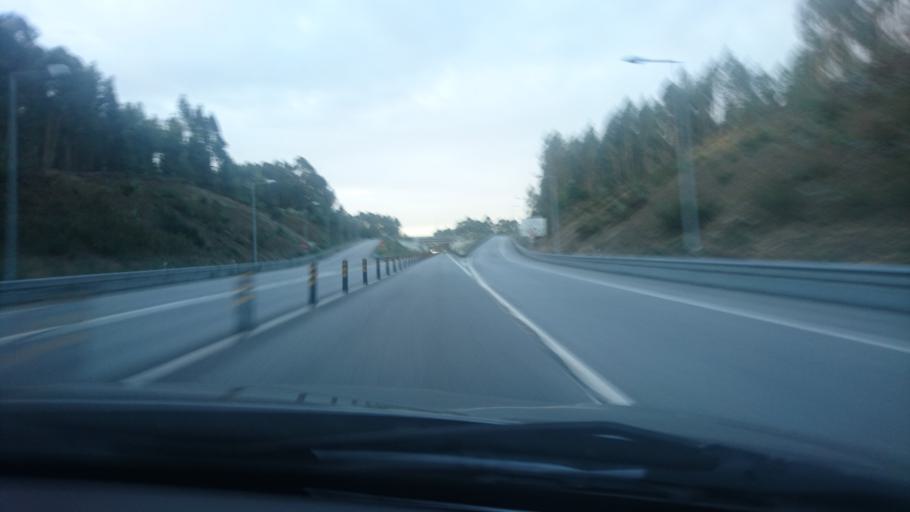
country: PT
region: Aveiro
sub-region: Santa Maria da Feira
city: Arrifana
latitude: 40.9266
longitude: -8.4856
